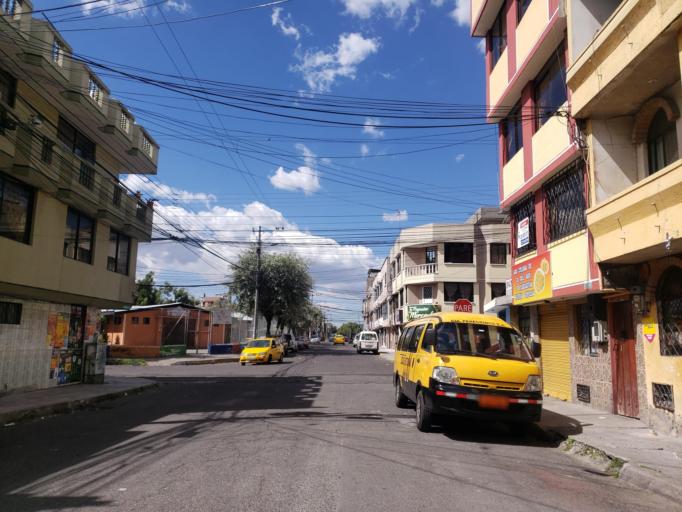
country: EC
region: Pichincha
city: Quito
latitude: -0.2711
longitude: -78.5382
